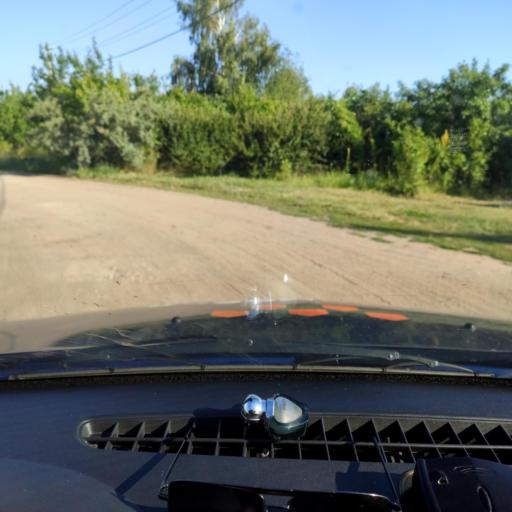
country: RU
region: Voronezj
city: Podgornoye
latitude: 51.8653
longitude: 39.1740
